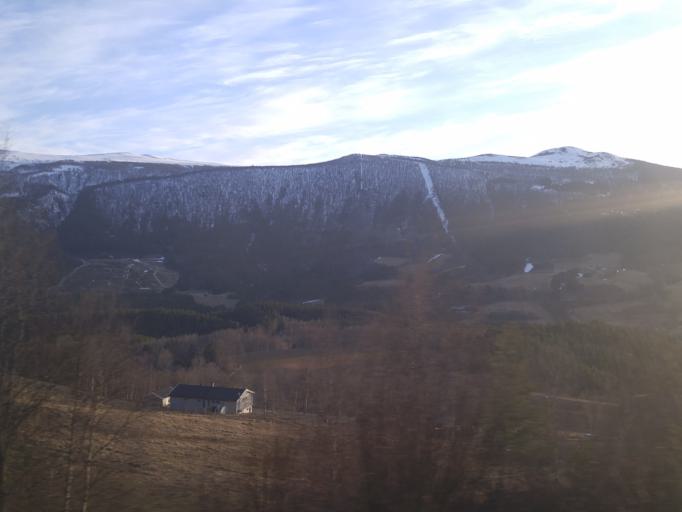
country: NO
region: Oppland
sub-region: Dovre
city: Dombas
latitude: 62.0620
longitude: 9.1277
